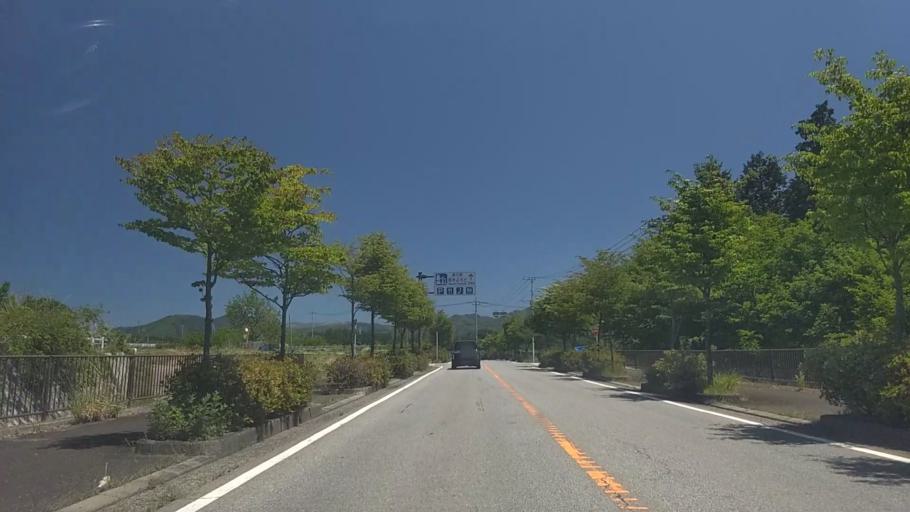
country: JP
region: Yamanashi
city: Nirasaki
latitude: 35.8395
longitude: 138.4321
